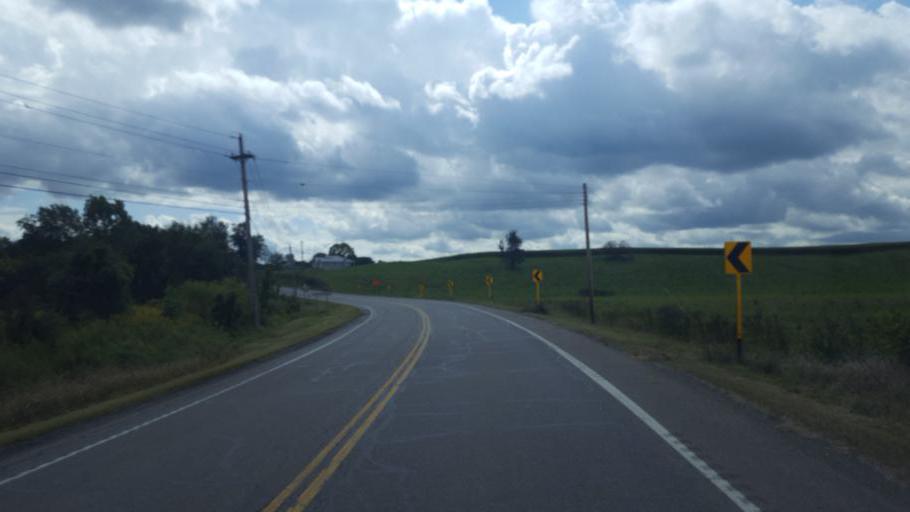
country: US
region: Ohio
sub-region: Richland County
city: Lincoln Heights
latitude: 40.8854
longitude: -82.5126
